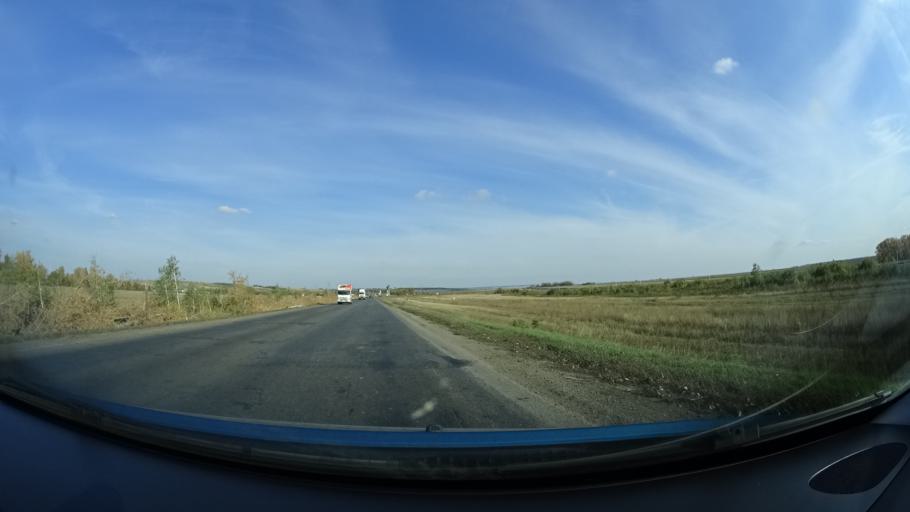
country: RU
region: Bashkortostan
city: Buzdyak
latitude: 54.6260
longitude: 54.4347
